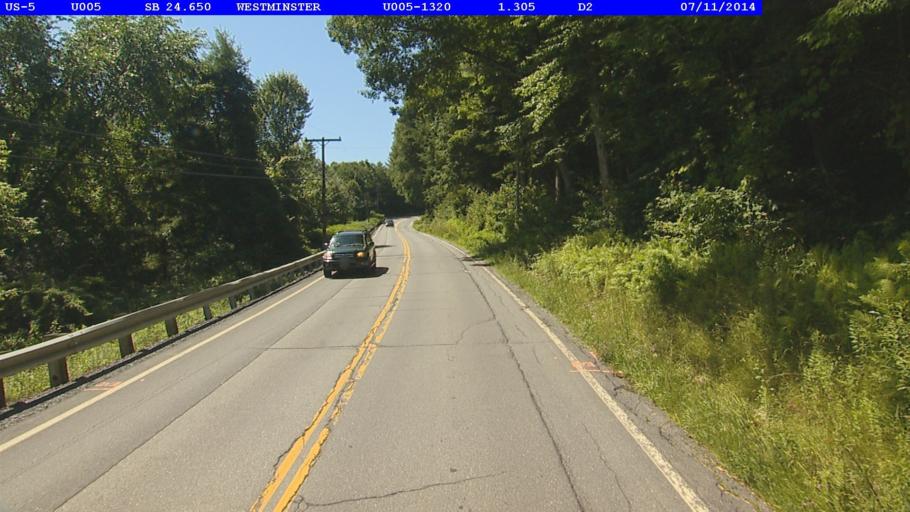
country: US
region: New Hampshire
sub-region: Cheshire County
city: Westmoreland
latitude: 43.0389
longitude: -72.4661
